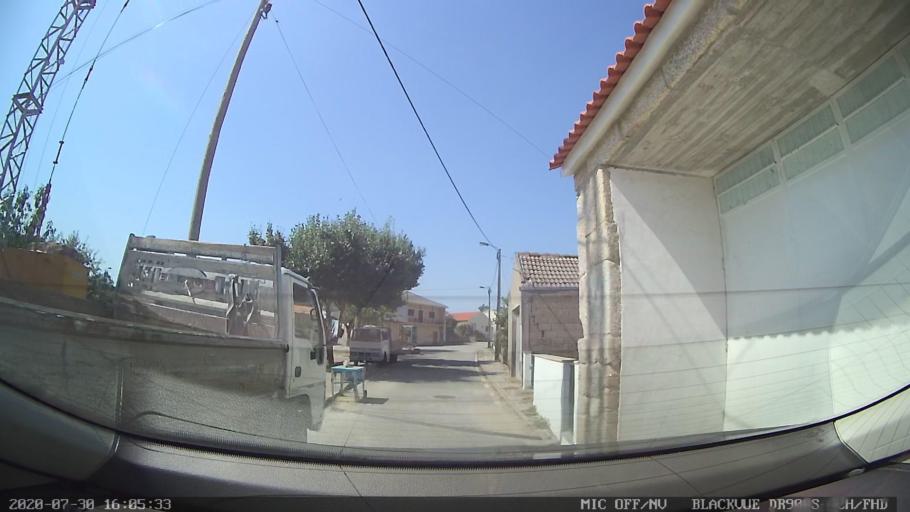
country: PT
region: Vila Real
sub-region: Murca
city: Murca
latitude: 41.3474
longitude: -7.4840
